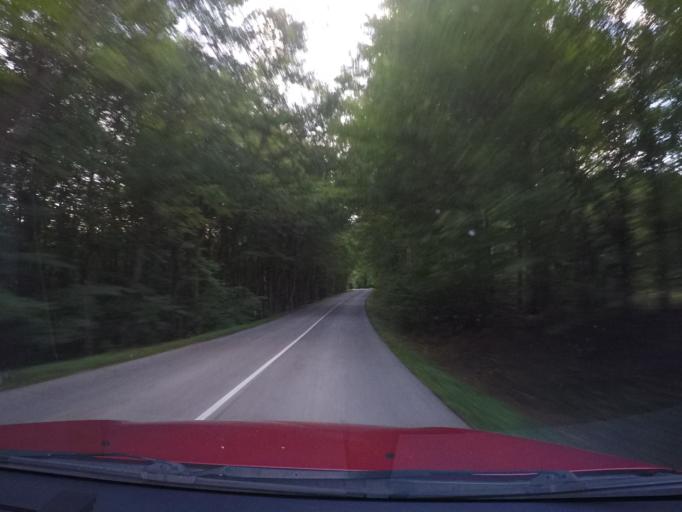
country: SK
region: Kosicky
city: Roznava
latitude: 48.6492
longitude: 20.6775
